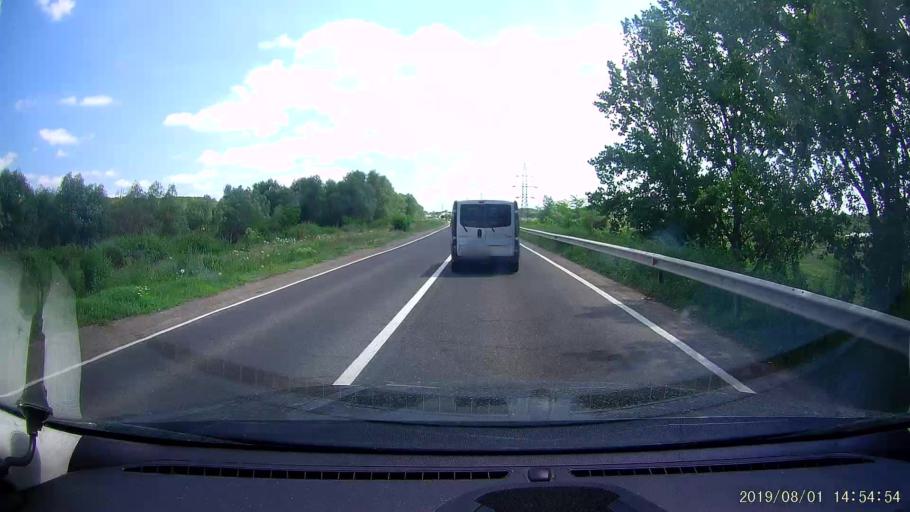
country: RO
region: Braila
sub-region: Municipiul Braila
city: Braila
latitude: 45.3116
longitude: 27.9832
